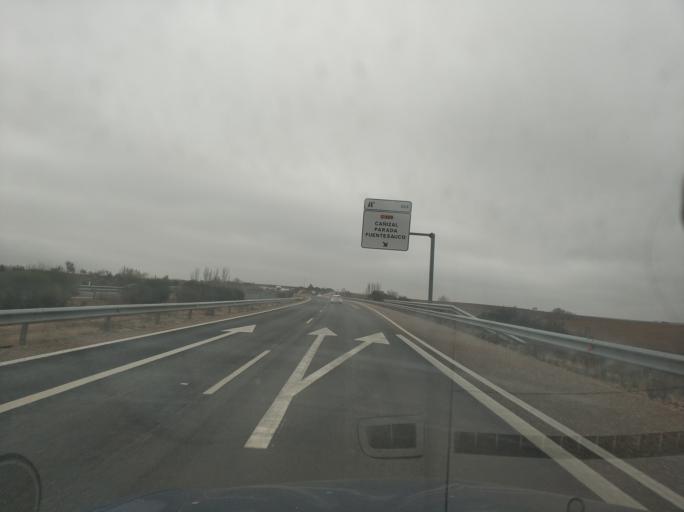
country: ES
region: Castille and Leon
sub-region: Provincia de Zamora
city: Canizal
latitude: 41.1785
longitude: -5.3695
